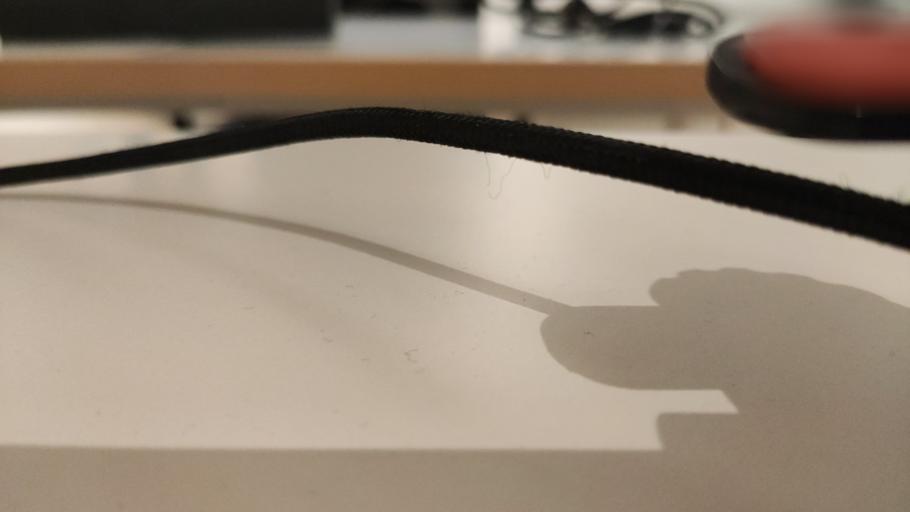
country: RU
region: Moskovskaya
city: Dorokhovo
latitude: 55.4205
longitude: 36.3620
